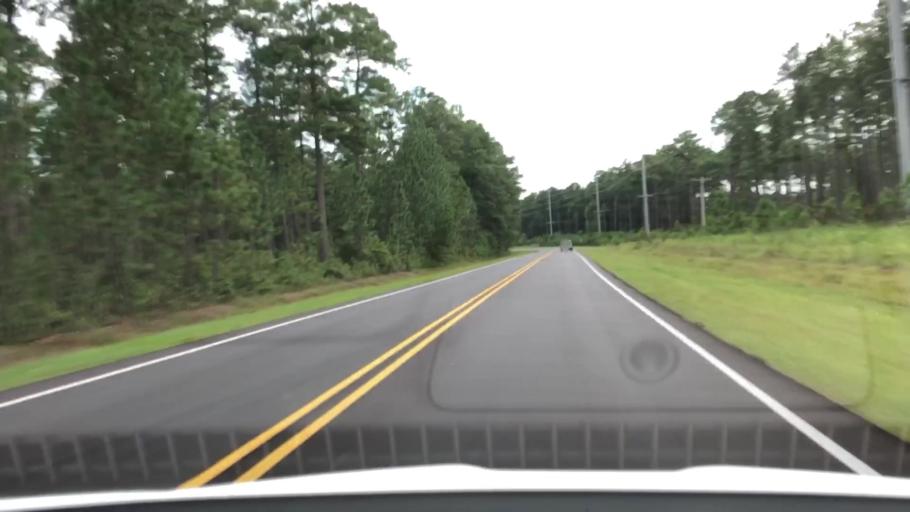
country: US
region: North Carolina
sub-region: Jones County
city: Maysville
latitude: 34.8191
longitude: -77.1471
